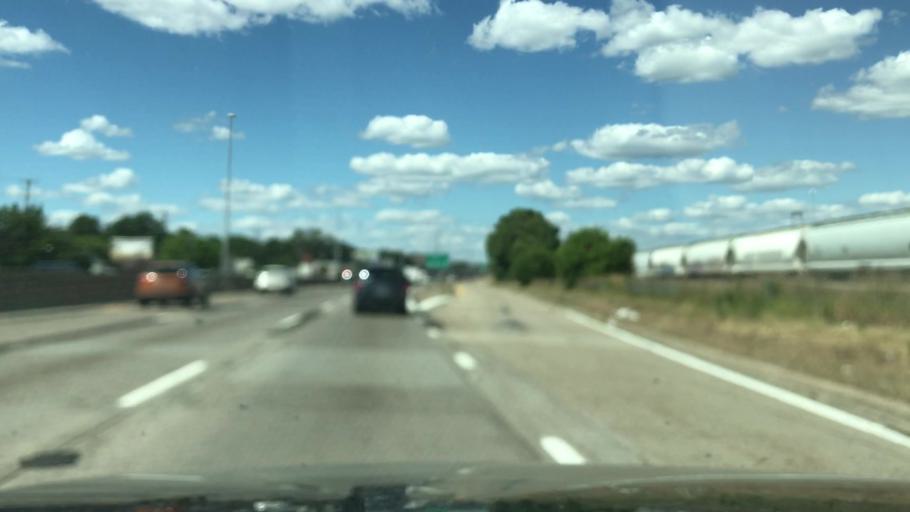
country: US
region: Michigan
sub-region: Kent County
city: Wyoming
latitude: 42.9337
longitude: -85.6807
